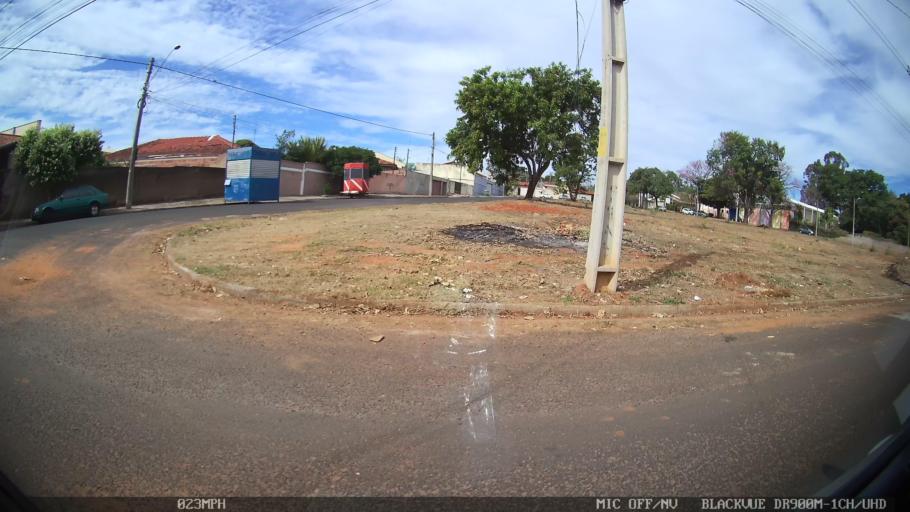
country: BR
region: Sao Paulo
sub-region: Catanduva
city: Catanduva
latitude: -21.1563
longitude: -48.9772
